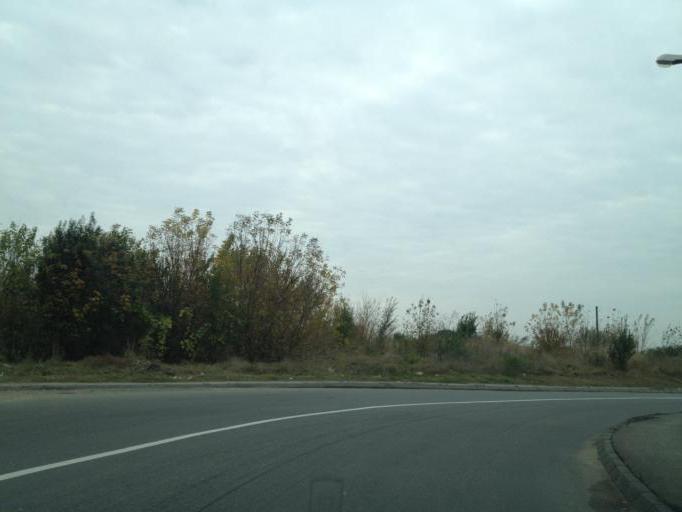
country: RO
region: Dolj
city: Craiova
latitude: 44.3004
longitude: 23.8195
